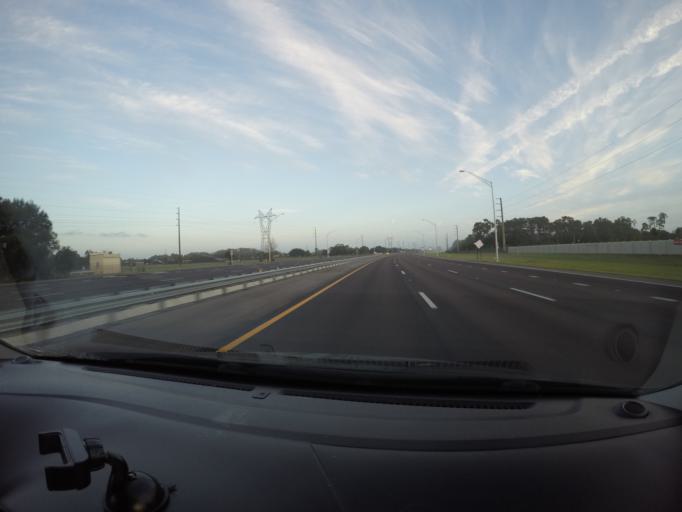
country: US
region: Florida
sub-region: Orange County
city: Azalea Park
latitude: 28.5159
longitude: -81.2501
